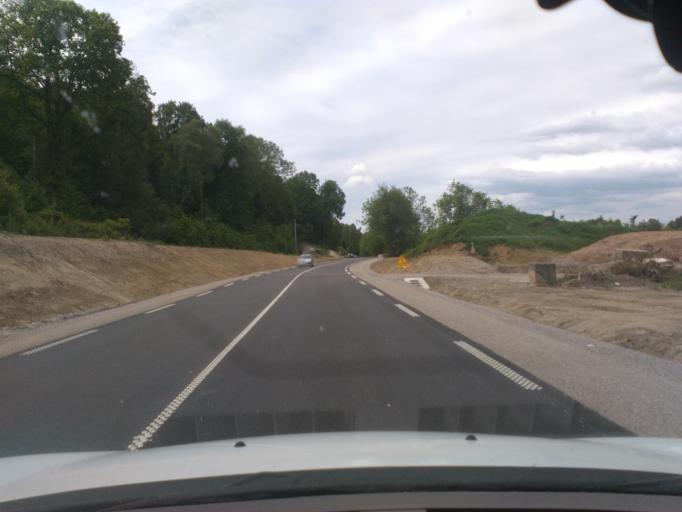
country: FR
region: Lorraine
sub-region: Departement des Vosges
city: Deyvillers
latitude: 48.1788
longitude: 6.4877
